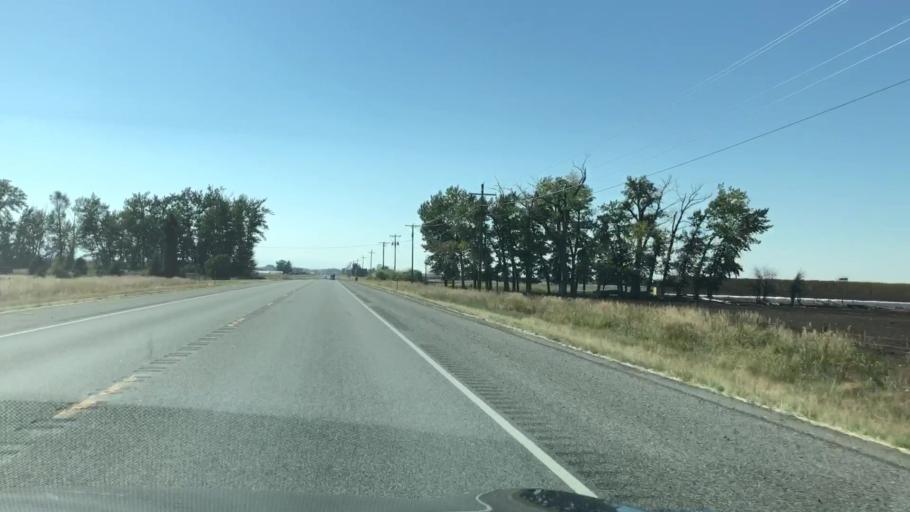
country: US
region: Montana
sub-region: Gallatin County
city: Belgrade
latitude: 45.7293
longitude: -111.1669
